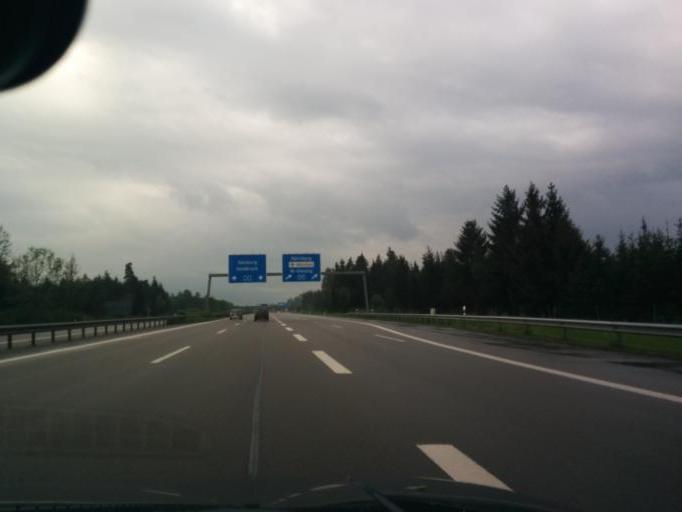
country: DE
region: Bavaria
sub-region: Upper Bavaria
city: Ottobrunn
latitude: 48.0336
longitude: 11.6542
